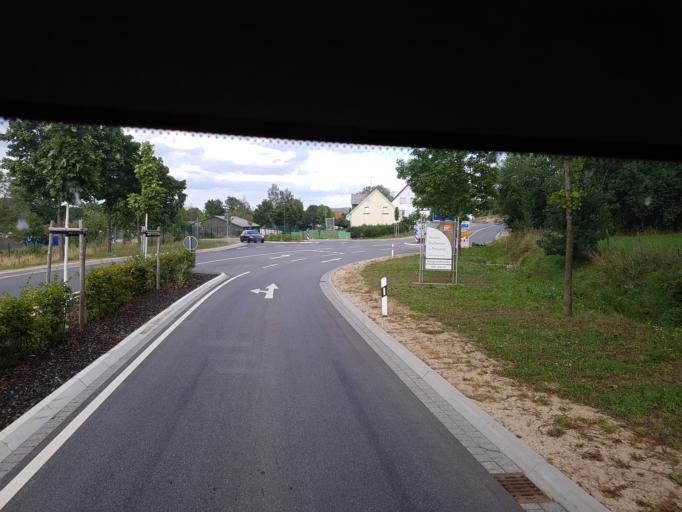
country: DE
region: Rheinland-Pfalz
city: Dockweiler
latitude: 50.2506
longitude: 6.7731
